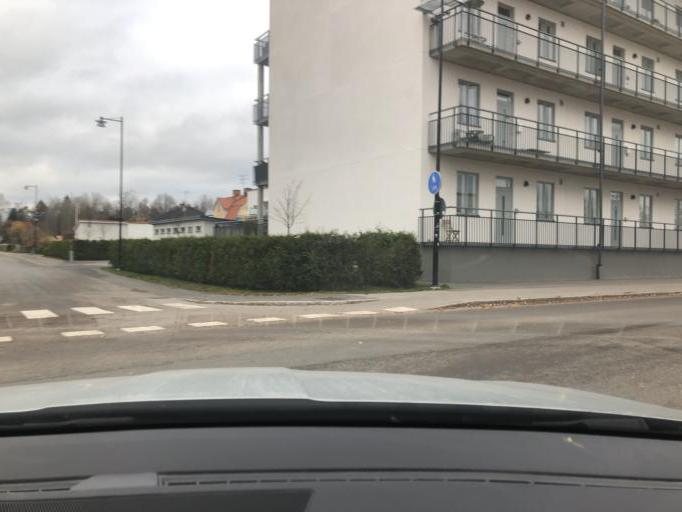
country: SE
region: Uppsala
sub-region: Tierps Kommun
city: Tierp
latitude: 60.3448
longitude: 17.5121
